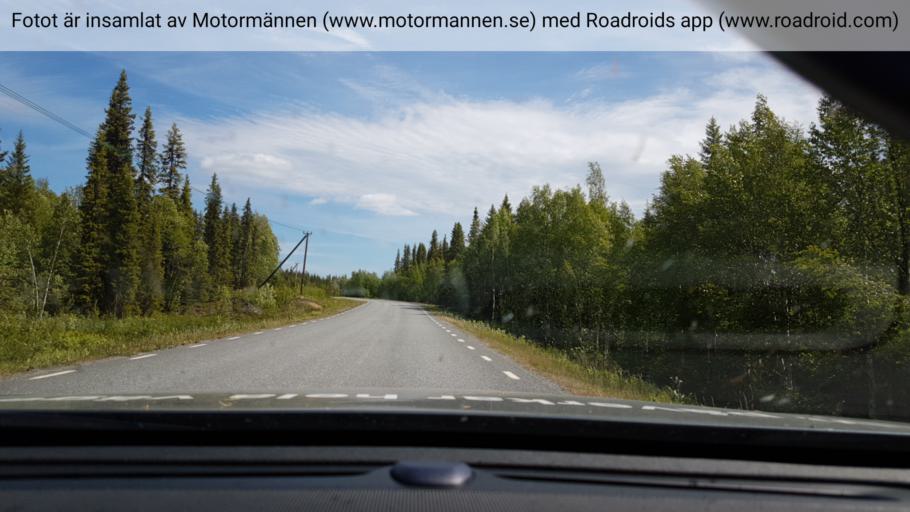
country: SE
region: Vaesterbotten
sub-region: Vilhelmina Kommun
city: Sjoberg
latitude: 65.2248
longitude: 15.9386
